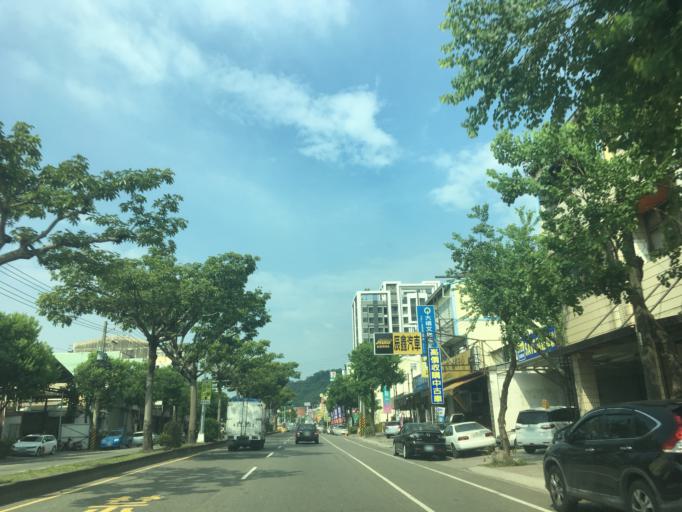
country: TW
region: Taiwan
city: Fengyuan
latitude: 24.2640
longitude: 120.7432
